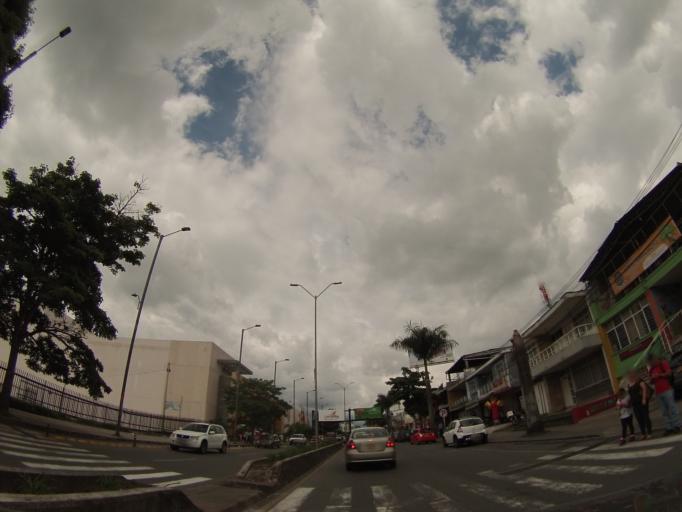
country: CO
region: Quindio
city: Armenia
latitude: 4.5395
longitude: -75.6659
